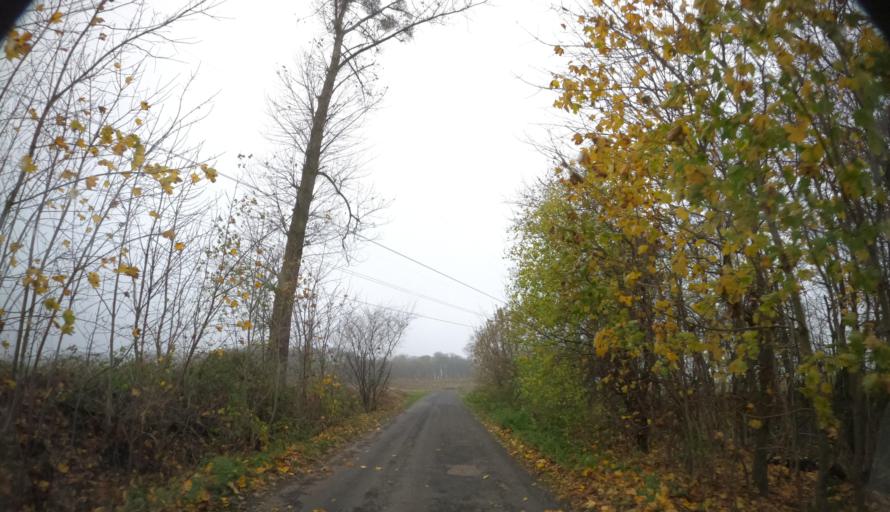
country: PL
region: West Pomeranian Voivodeship
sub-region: Powiat lobeski
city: Radowo Male
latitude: 53.6712
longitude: 15.4480
